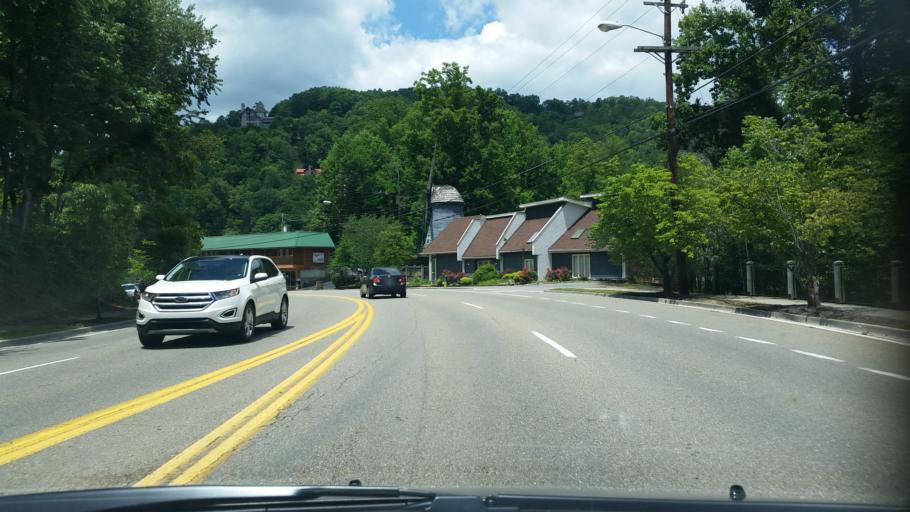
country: US
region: Tennessee
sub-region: Sevier County
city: Gatlinburg
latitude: 35.7162
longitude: -83.5082
